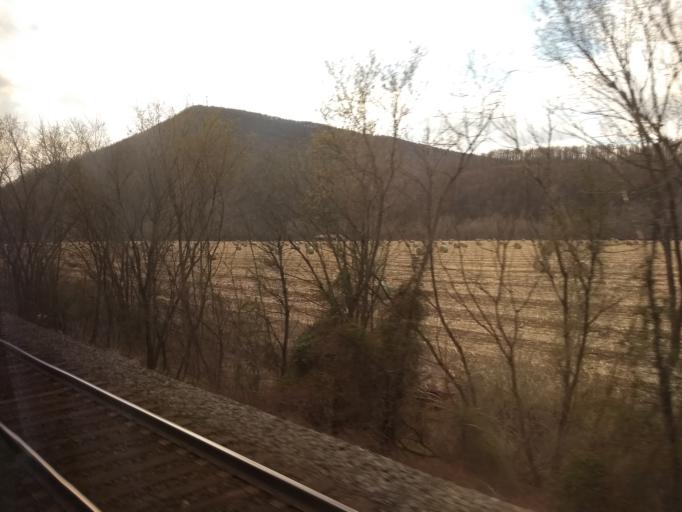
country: US
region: Pennsylvania
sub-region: Huntingdon County
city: Huntingdon
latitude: 40.4525
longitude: -77.9686
